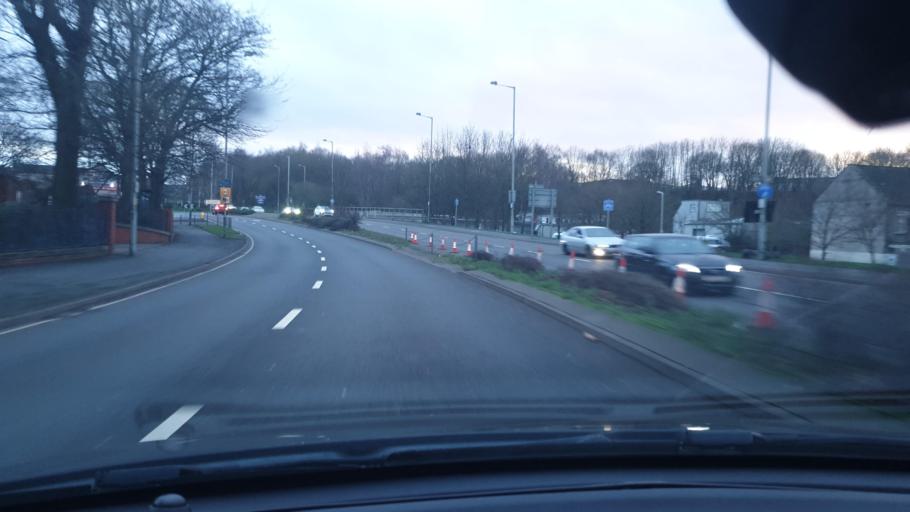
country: GB
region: England
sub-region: Wolverhampton
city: Wolverhampton
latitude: 52.6033
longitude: -2.1304
